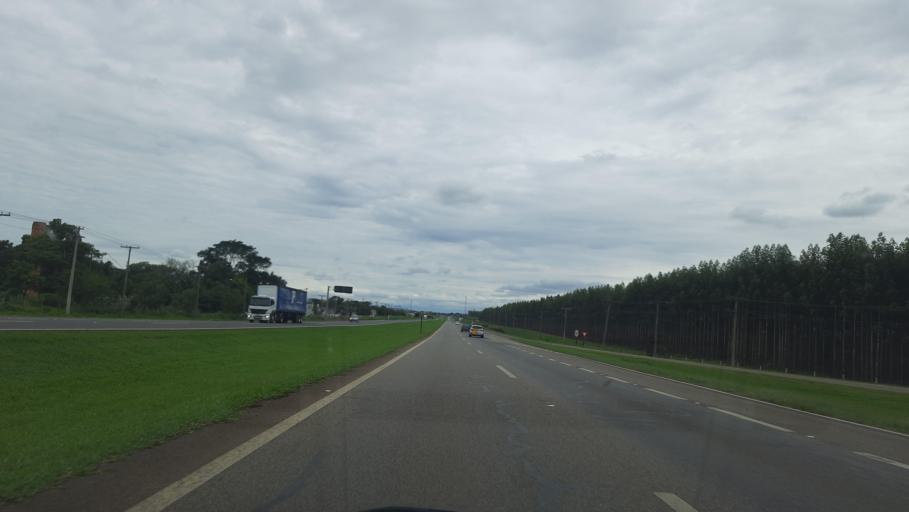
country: BR
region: Sao Paulo
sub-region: Moji-Guacu
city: Mogi-Gaucu
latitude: -22.3229
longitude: -46.9624
